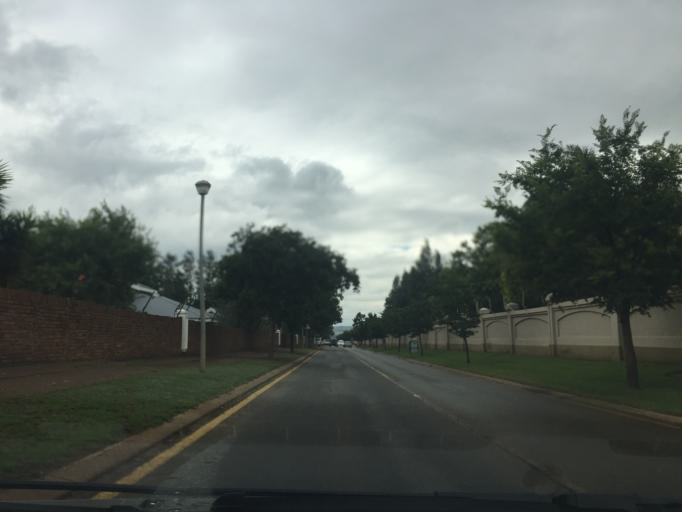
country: ZA
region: Gauteng
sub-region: City of Tshwane Metropolitan Municipality
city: Pretoria
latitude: -25.7779
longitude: 28.3706
